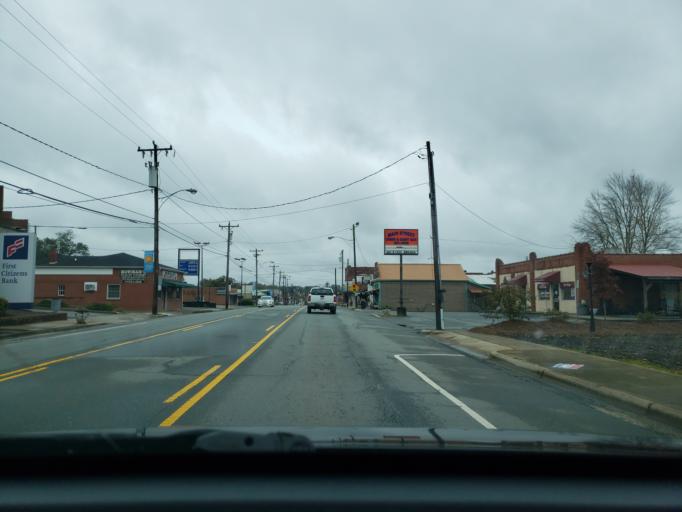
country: US
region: North Carolina
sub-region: Stokes County
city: Walnut Cove
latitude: 36.2979
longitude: -80.1417
